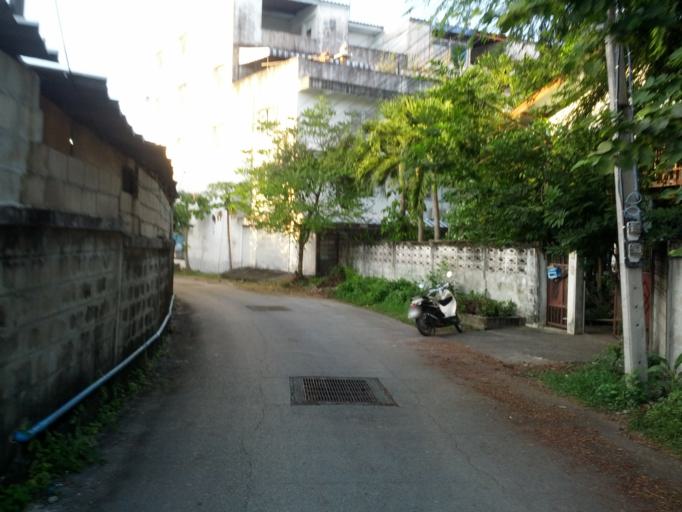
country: TH
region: Lampang
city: Lampang
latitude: 18.2900
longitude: 99.5112
